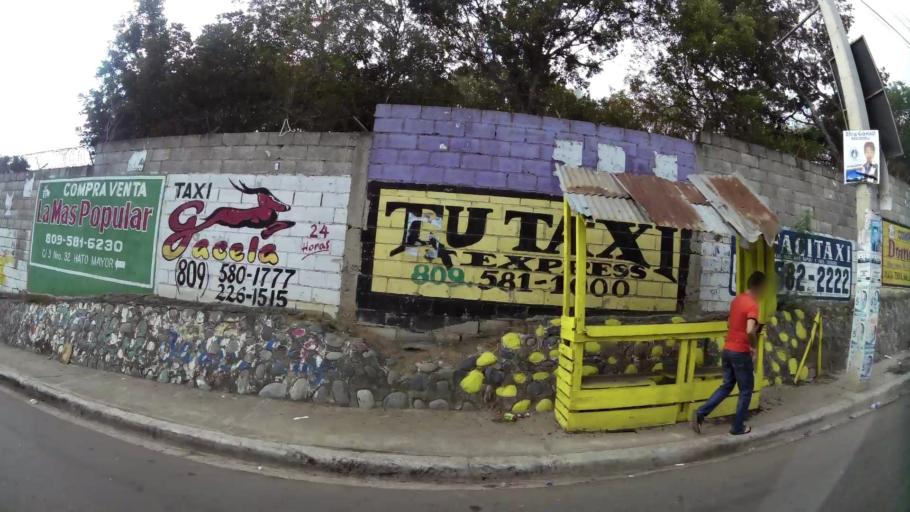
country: DO
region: Santiago
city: Santiago de los Caballeros
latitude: 19.4283
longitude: -70.6797
